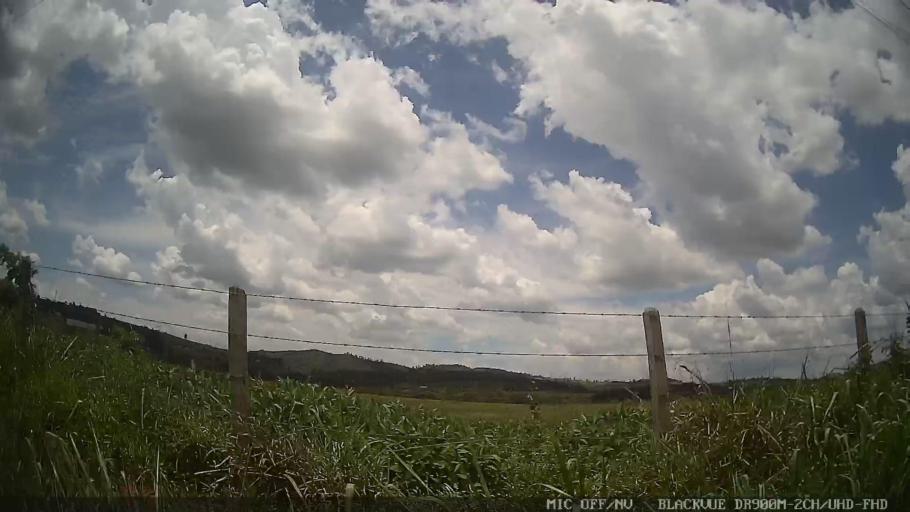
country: BR
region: Sao Paulo
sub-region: Atibaia
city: Atibaia
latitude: -23.1040
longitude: -46.6263
